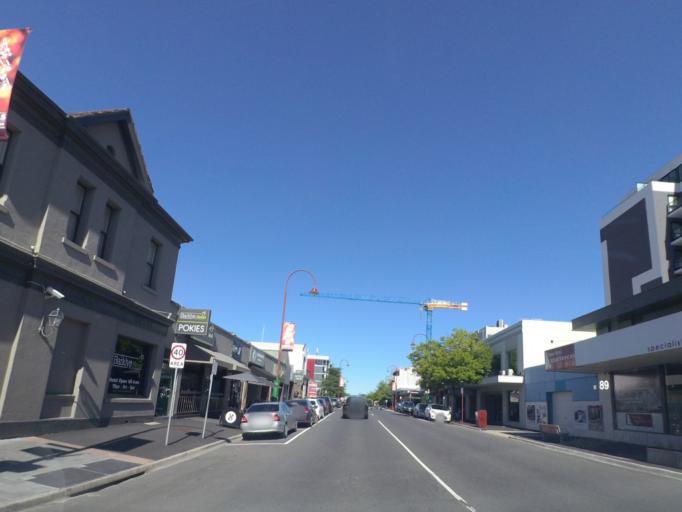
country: AU
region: Victoria
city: Rosanna
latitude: -37.7564
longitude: 145.0672
